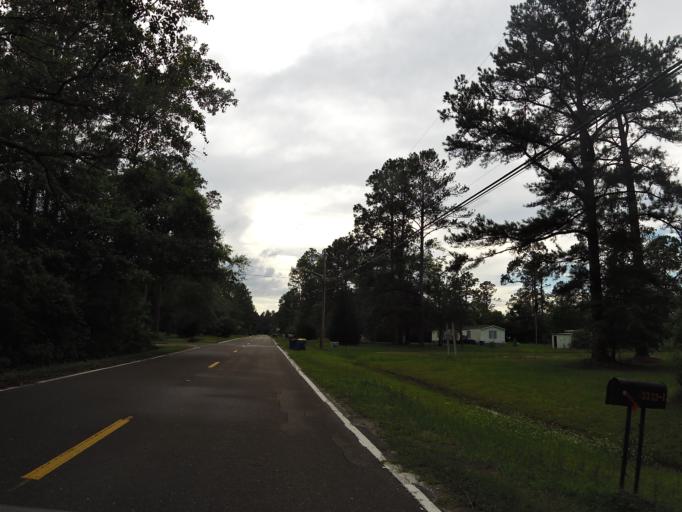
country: US
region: Florida
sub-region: Nassau County
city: Nassau Village-Ratliff
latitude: 30.5506
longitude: -81.7003
